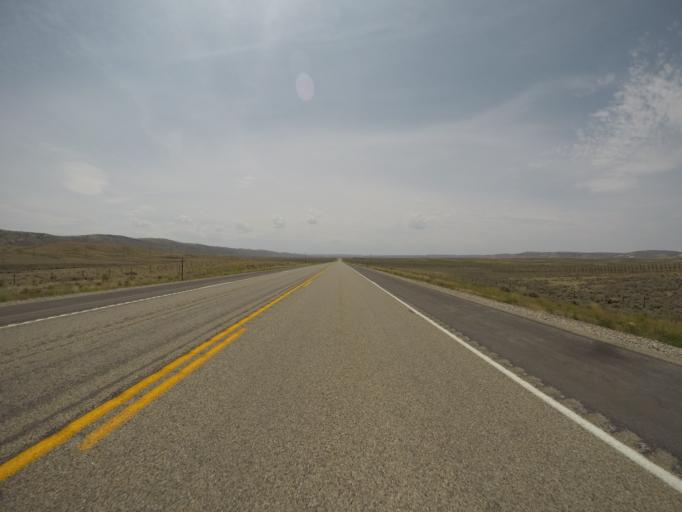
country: US
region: Wyoming
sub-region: Lincoln County
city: Kemmerer
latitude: 41.6916
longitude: -110.5671
